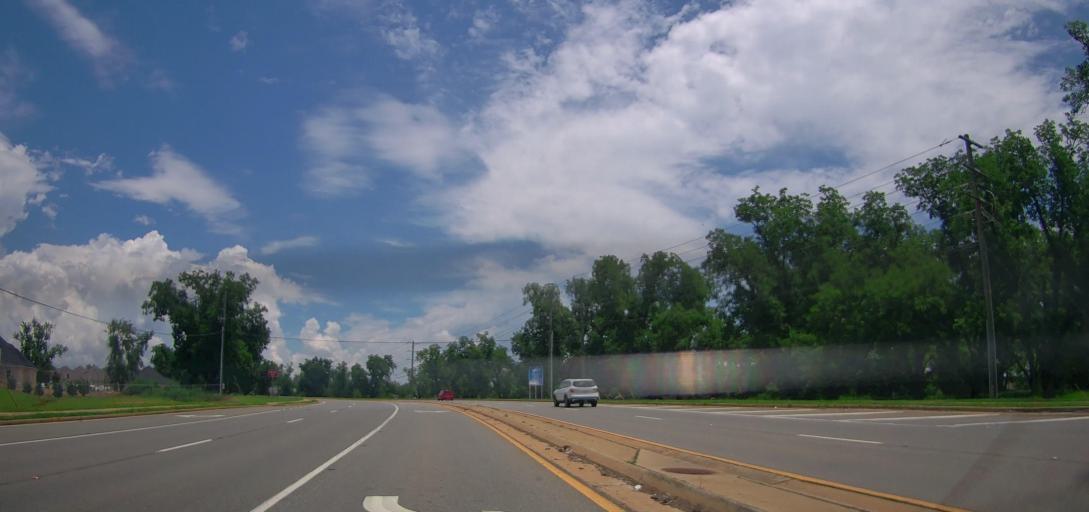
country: US
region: Georgia
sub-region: Houston County
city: Perry
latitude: 32.4989
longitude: -83.6658
